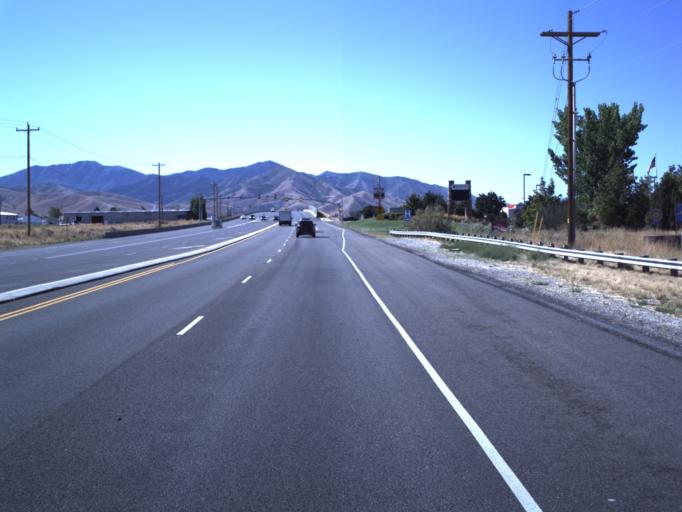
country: US
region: Utah
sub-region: Tooele County
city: Tooele
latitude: 40.5681
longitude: -112.2958
